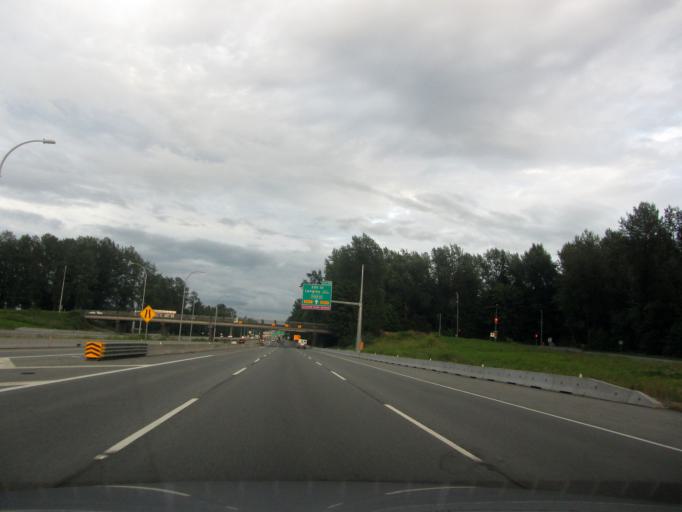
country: CA
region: British Columbia
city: Pitt Meadows
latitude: 49.1706
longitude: -122.6944
